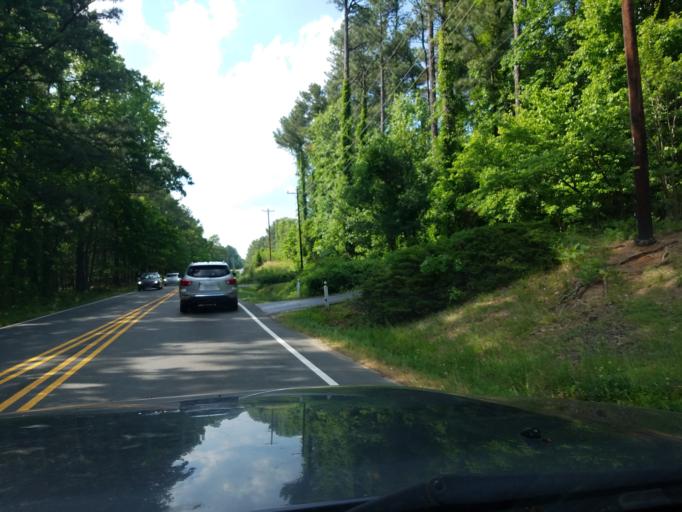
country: US
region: North Carolina
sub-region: Durham County
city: Durham
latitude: 35.9373
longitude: -78.9633
